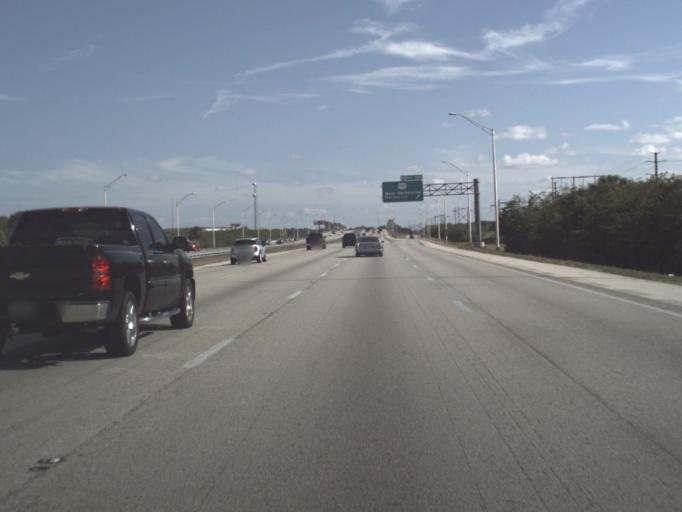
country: US
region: Florida
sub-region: Brevard County
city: June Park
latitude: 28.0872
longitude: -80.7062
